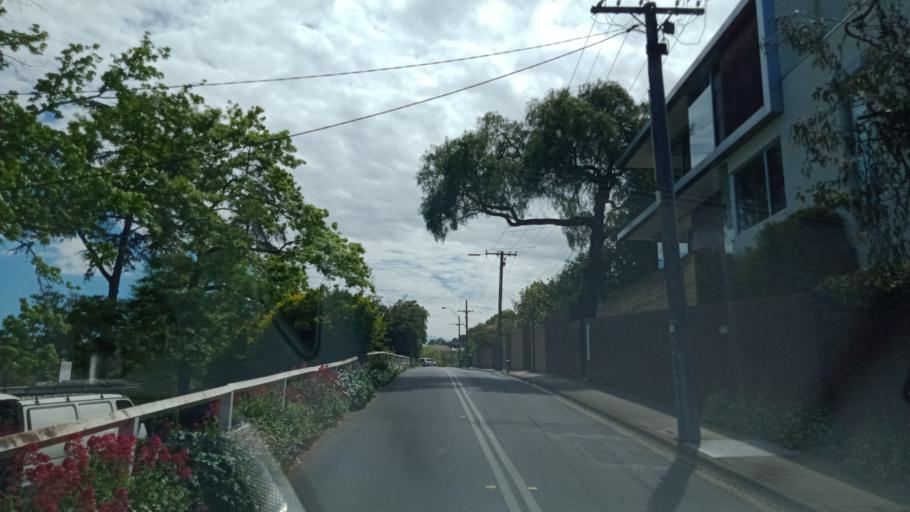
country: AU
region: Victoria
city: Toorak
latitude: -37.8316
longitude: 145.0294
